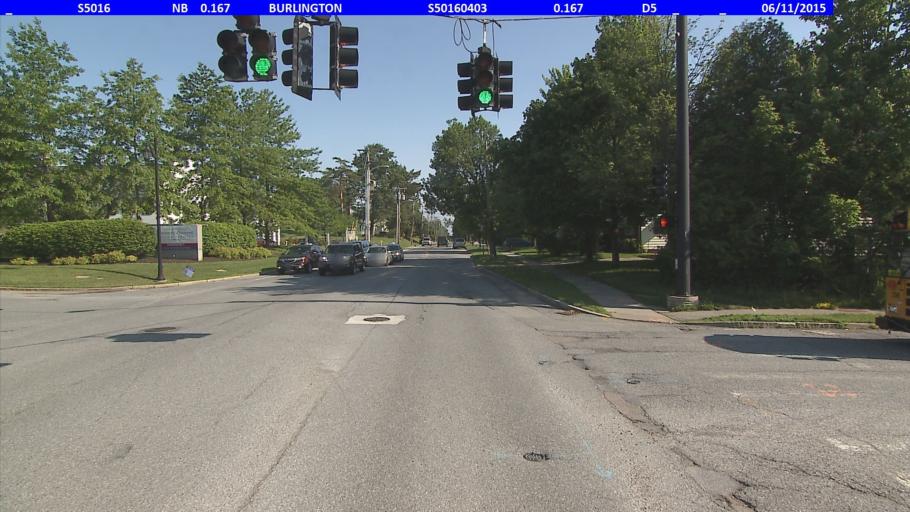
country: US
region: Vermont
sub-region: Chittenden County
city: Winooski
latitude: 44.4750
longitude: -73.1907
